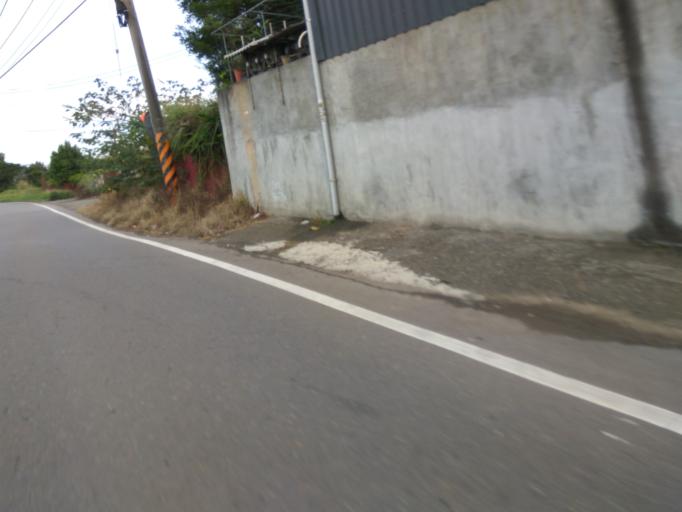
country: TW
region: Taiwan
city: Daxi
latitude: 24.9469
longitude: 121.1447
